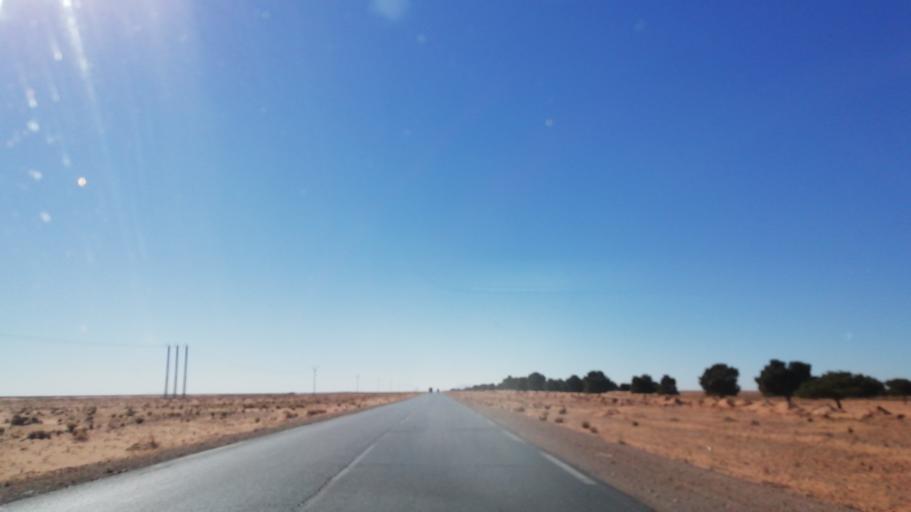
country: DZ
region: Wilaya de Naama
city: Naama
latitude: 33.9748
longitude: 0.0238
